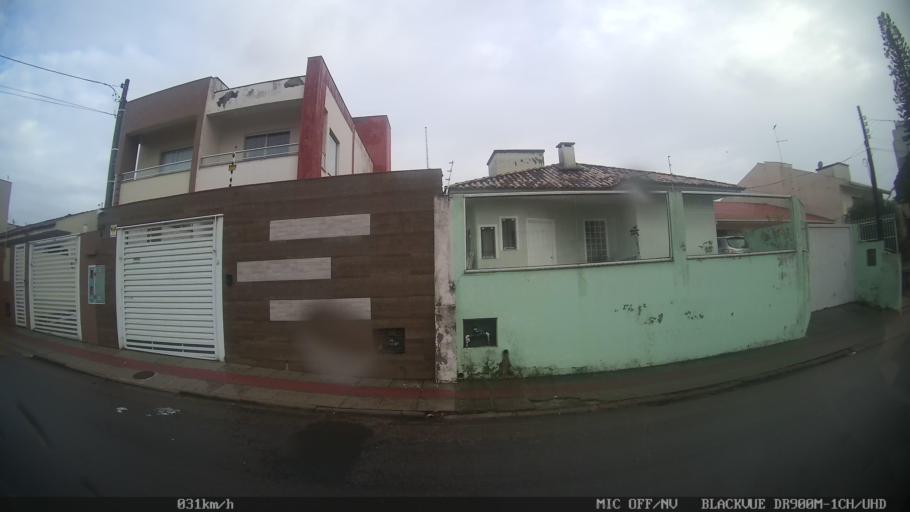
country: BR
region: Santa Catarina
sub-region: Sao Jose
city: Campinas
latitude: -27.5750
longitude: -48.6079
